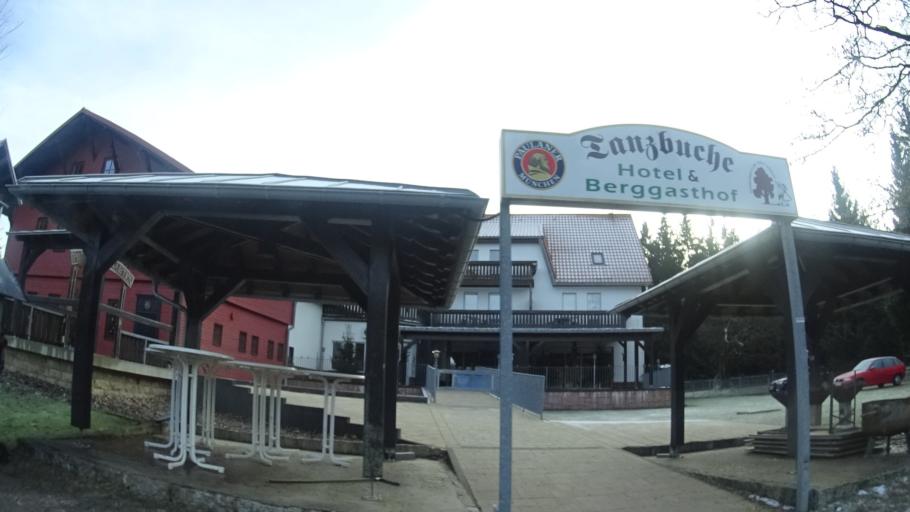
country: DE
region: Thuringia
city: Tabarz
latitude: 50.8428
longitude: 10.5231
